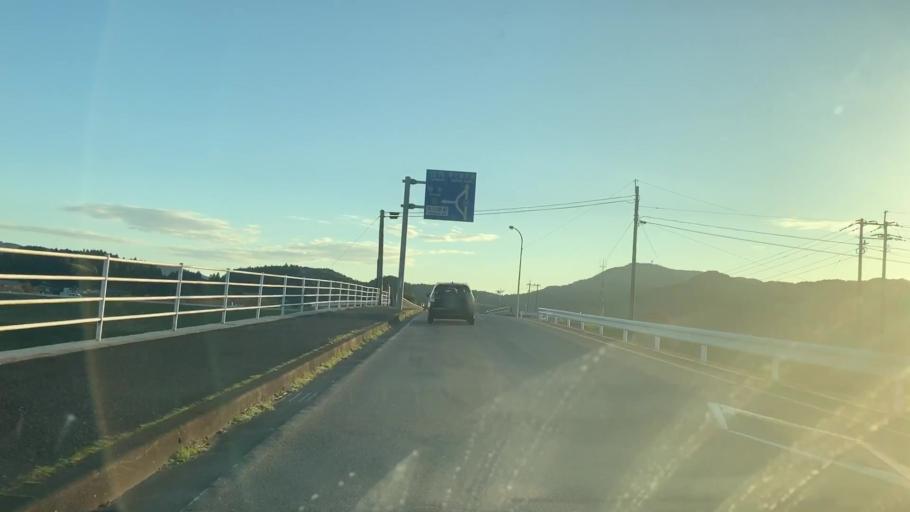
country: JP
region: Saga Prefecture
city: Imaricho-ko
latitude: 33.3095
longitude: 129.9708
